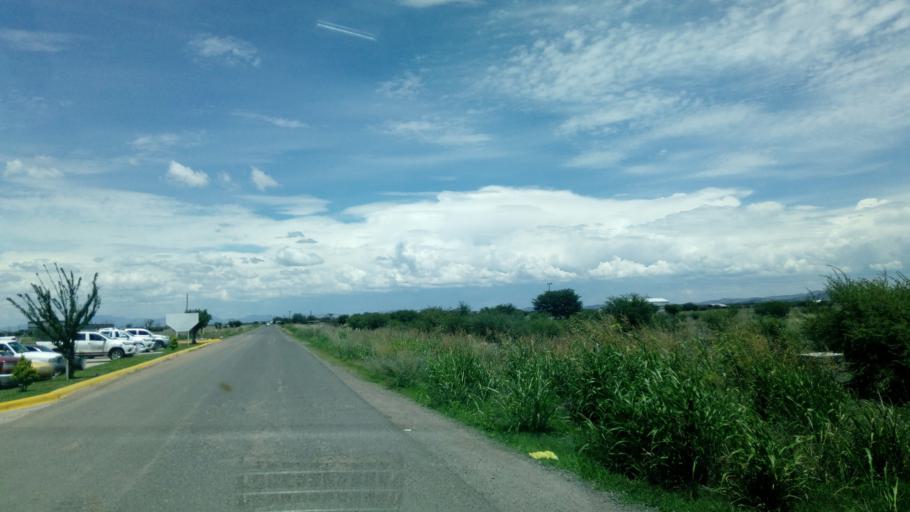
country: MX
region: Durango
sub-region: Durango
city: Jose Refugio Salcido
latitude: 24.1647
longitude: -104.5017
